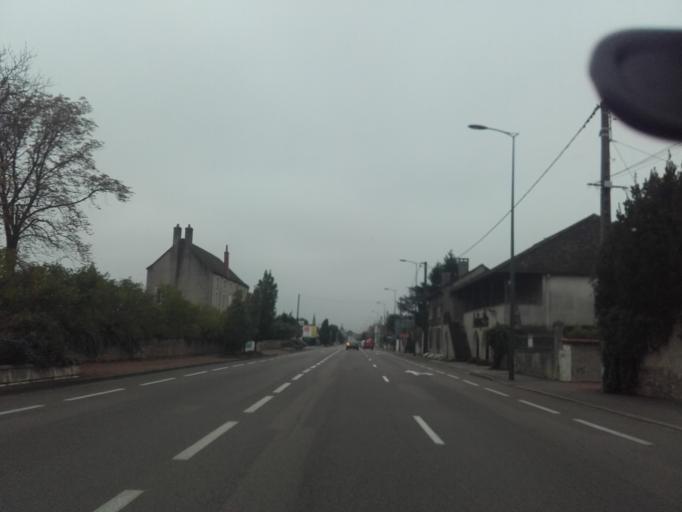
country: FR
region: Bourgogne
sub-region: Departement de la Cote-d'Or
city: Beaune
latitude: 47.0373
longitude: 4.8472
